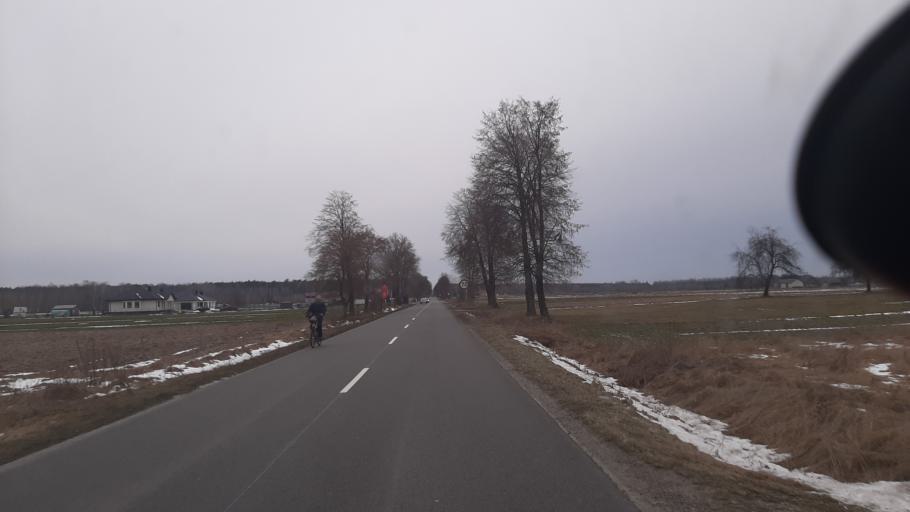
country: PL
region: Lublin Voivodeship
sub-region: Powiat lubartowski
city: Kamionka
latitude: 51.4940
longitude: 22.4248
